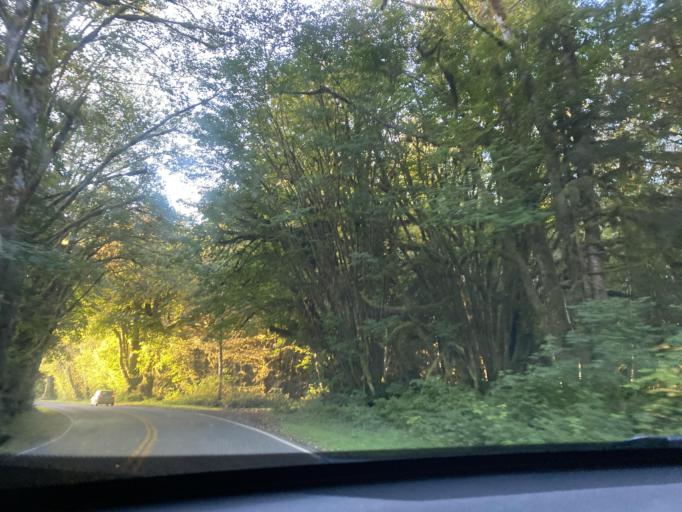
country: US
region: Washington
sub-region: Clallam County
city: Forks
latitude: 47.8175
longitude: -124.1713
